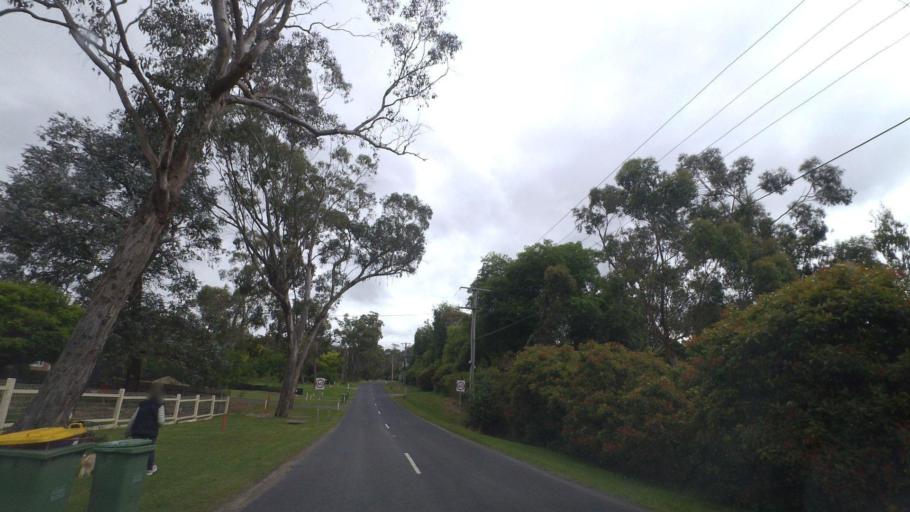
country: AU
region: Victoria
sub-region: Yarra Ranges
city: Mount Evelyn
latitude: -37.7788
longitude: 145.4192
